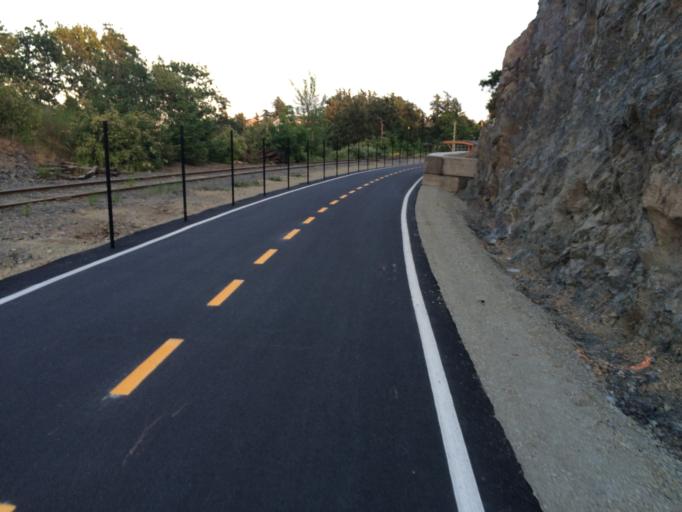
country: CA
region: British Columbia
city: Colwood
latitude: 48.4549
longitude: -123.4309
